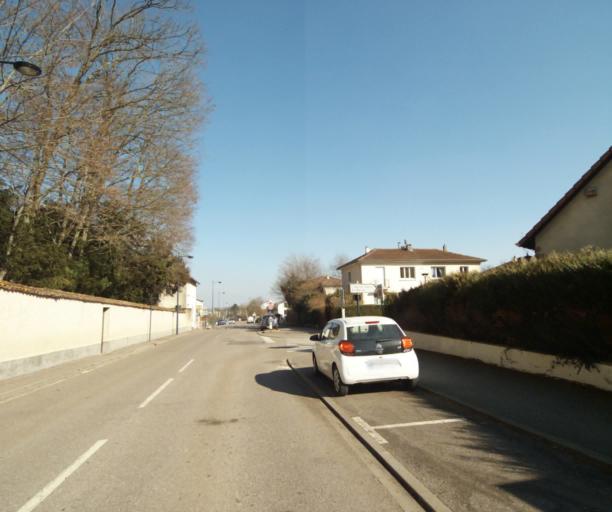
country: FR
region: Lorraine
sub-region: Departement de Meurthe-et-Moselle
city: Vandoeuvre-les-Nancy
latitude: 48.6451
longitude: 6.1779
